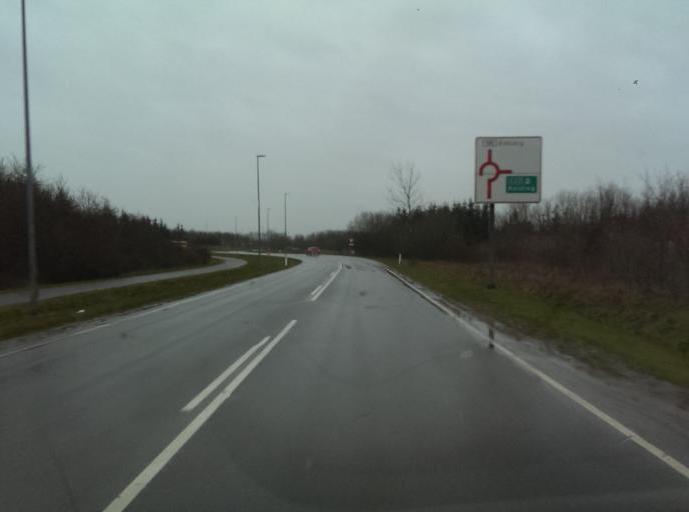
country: DK
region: South Denmark
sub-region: Esbjerg Kommune
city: Esbjerg
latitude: 55.4864
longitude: 8.5096
